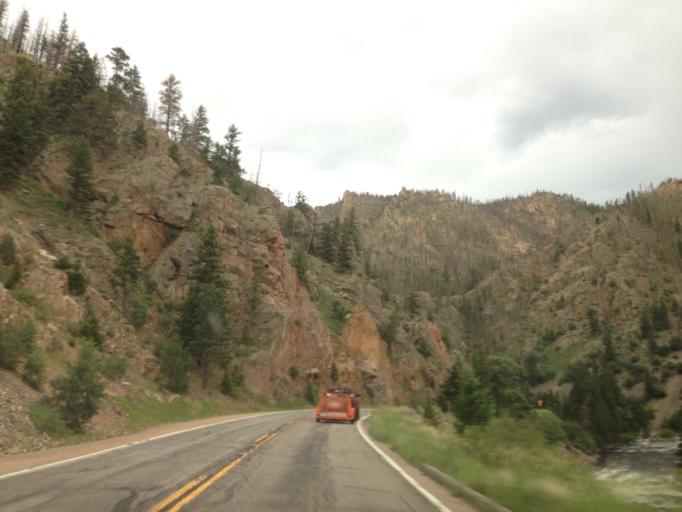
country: US
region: Colorado
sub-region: Larimer County
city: Laporte
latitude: 40.6835
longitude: -105.4342
